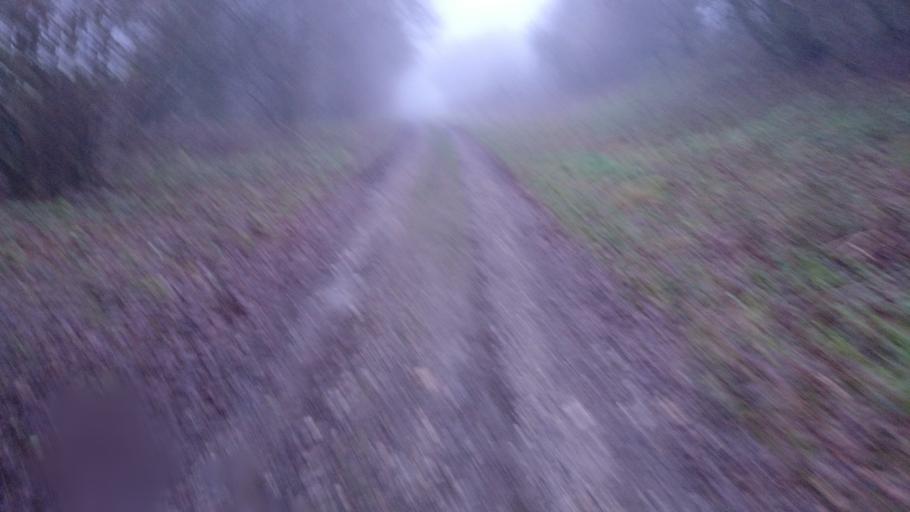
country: GB
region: England
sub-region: Hampshire
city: Basingstoke
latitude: 51.1991
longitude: -1.1306
